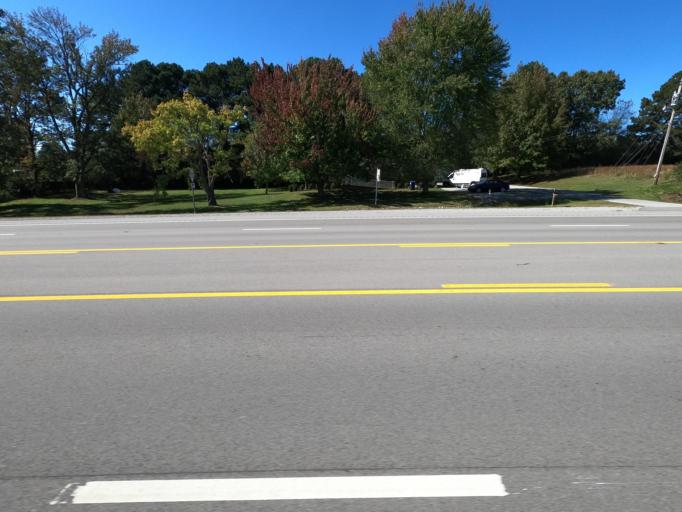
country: US
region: Tennessee
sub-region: Maury County
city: Mount Pleasant
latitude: 35.4289
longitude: -87.2812
